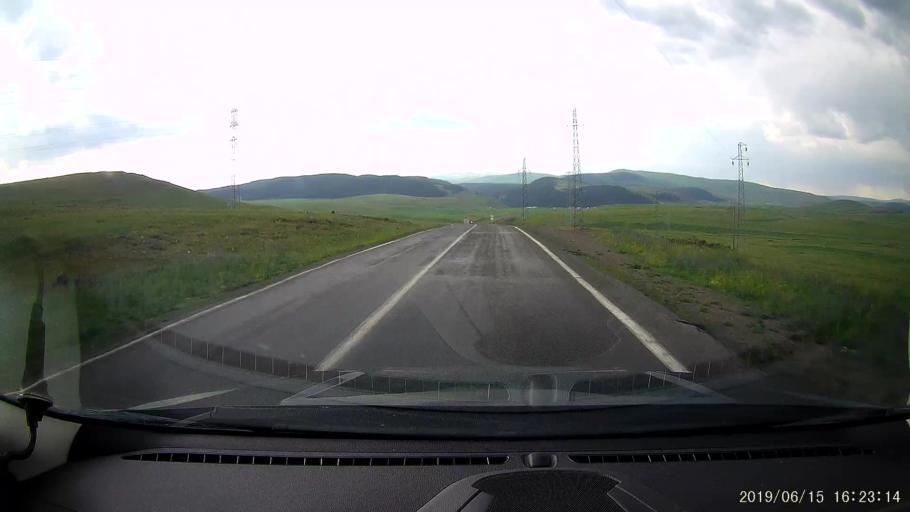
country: TR
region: Ardahan
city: Hanak
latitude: 41.1801
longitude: 42.8599
